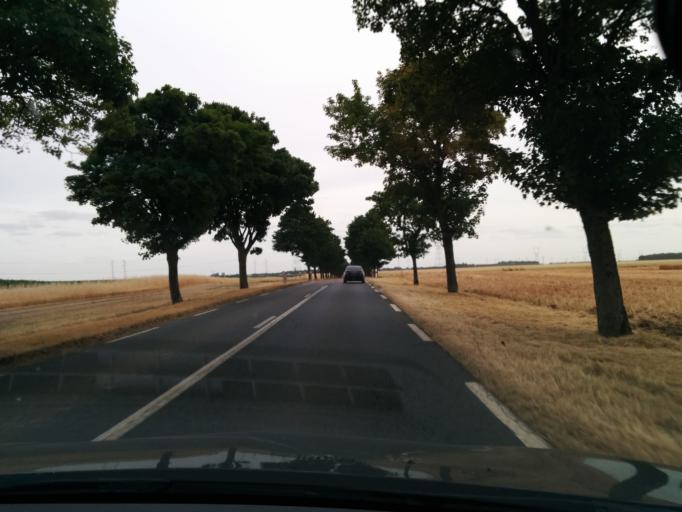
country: FR
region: Ile-de-France
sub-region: Departement de l'Essonne
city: Pussay
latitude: 48.3423
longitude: 1.9890
